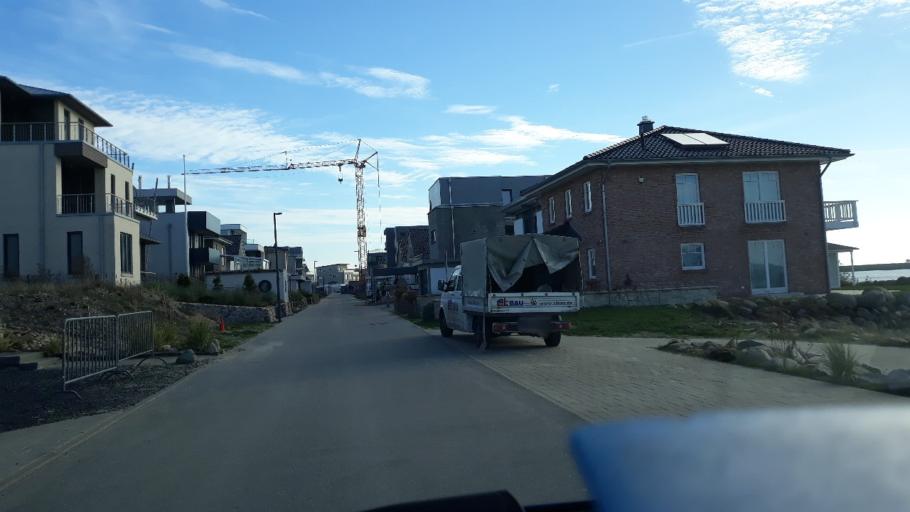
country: DE
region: Schleswig-Holstein
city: Maasholm
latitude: 54.6624
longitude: 10.0360
